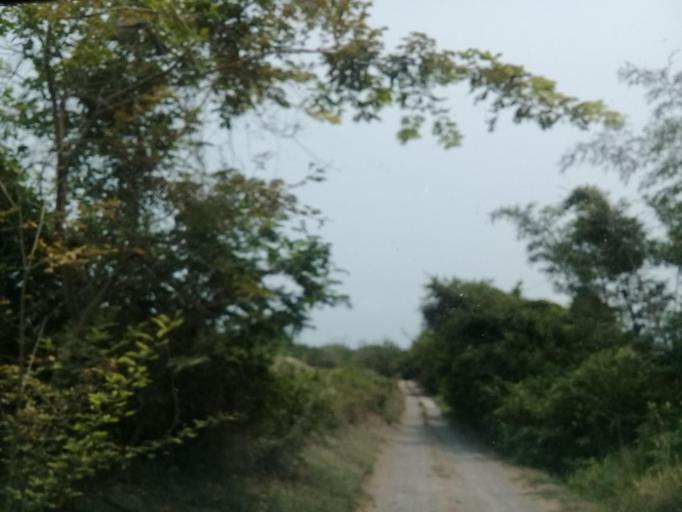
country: MX
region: Veracruz
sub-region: Veracruz
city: Hacienda Sotavento
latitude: 19.1418
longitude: -96.1590
